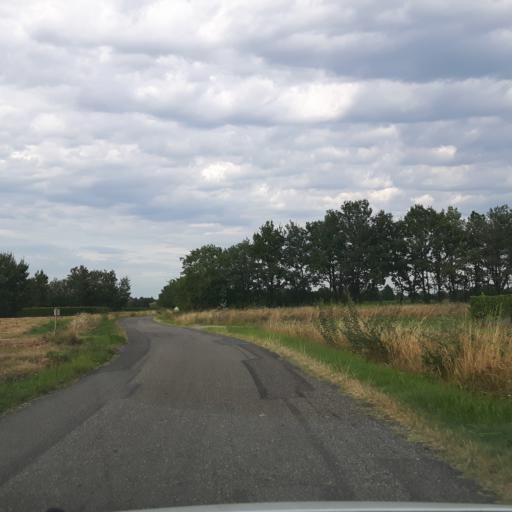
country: FR
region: Midi-Pyrenees
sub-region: Departement de la Haute-Garonne
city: Fronton
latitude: 43.8194
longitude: 1.3616
